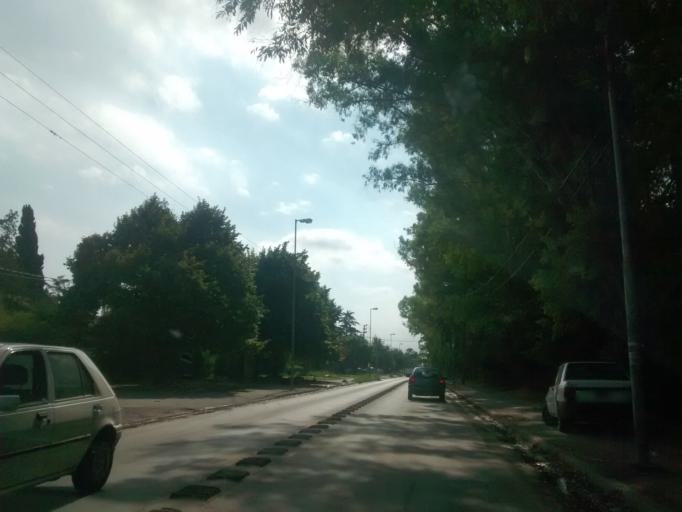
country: AR
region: Buenos Aires
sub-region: Partido de La Plata
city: La Plata
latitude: -34.9568
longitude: -57.8943
